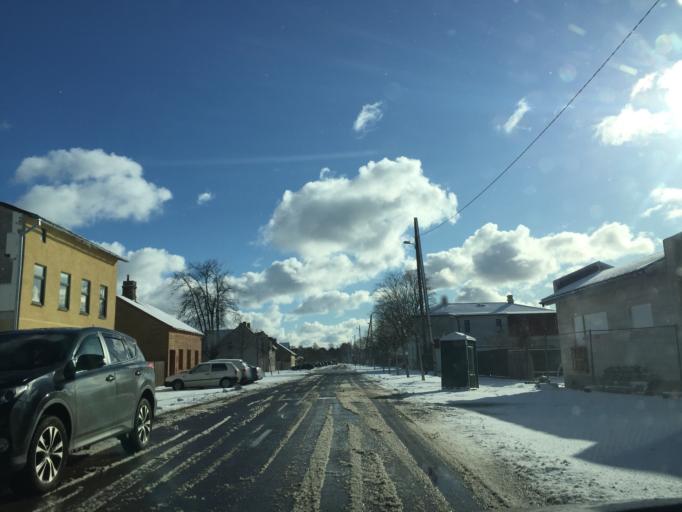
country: LV
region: Ventspils
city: Ventspils
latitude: 57.3837
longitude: 21.5567
